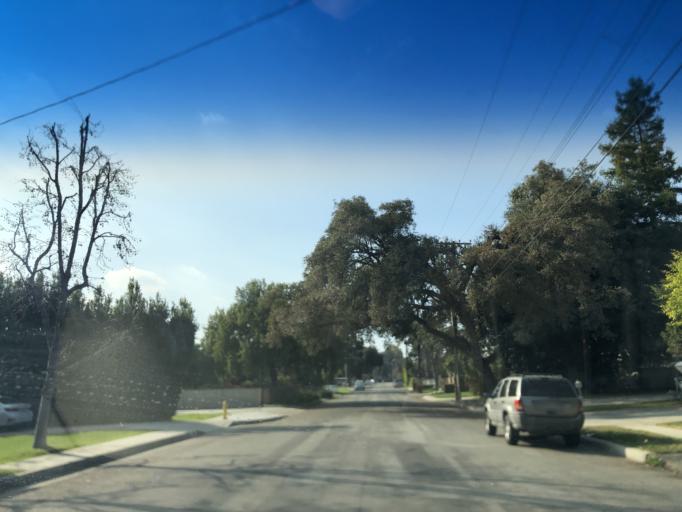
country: US
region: California
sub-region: Los Angeles County
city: East San Gabriel
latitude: 34.1110
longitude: -118.0877
